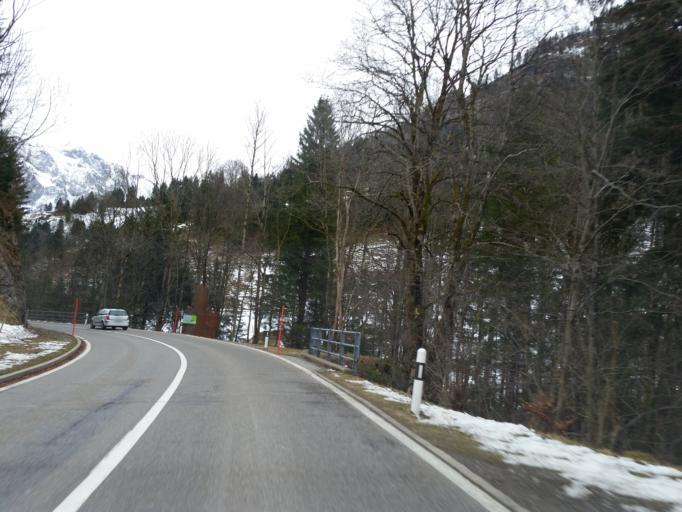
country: CH
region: Appenzell Ausserrhoden
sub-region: Bezirk Hinterland
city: Urnasch
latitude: 47.2808
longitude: 9.2774
